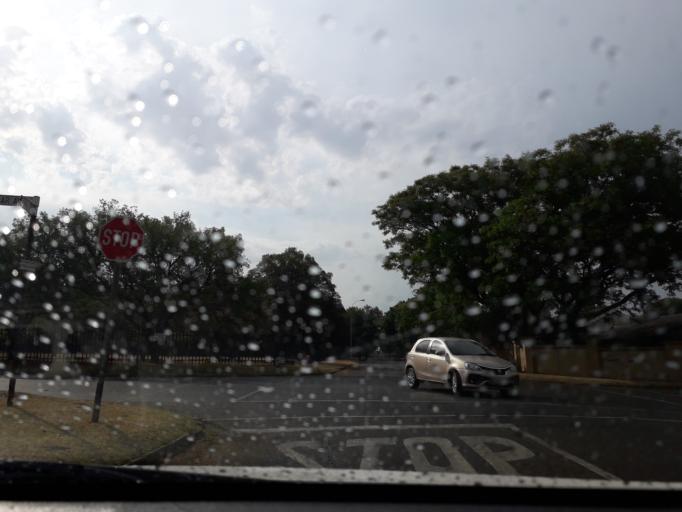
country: ZA
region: Gauteng
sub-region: City of Johannesburg Metropolitan Municipality
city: Modderfontein
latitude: -26.0910
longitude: 28.2449
